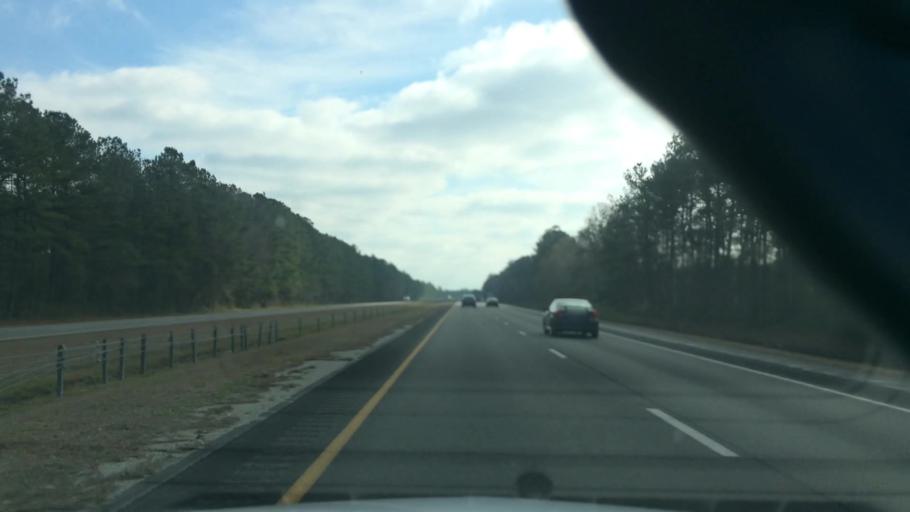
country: US
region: North Carolina
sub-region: Pender County
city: Burgaw
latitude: 34.5979
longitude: -77.9116
